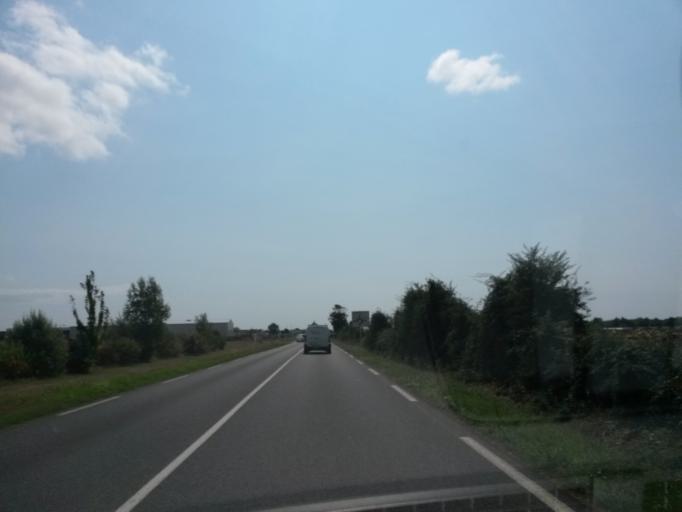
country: FR
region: Pays de la Loire
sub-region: Departement de la Vendee
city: Jard-sur-Mer
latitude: 46.4274
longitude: -1.5751
